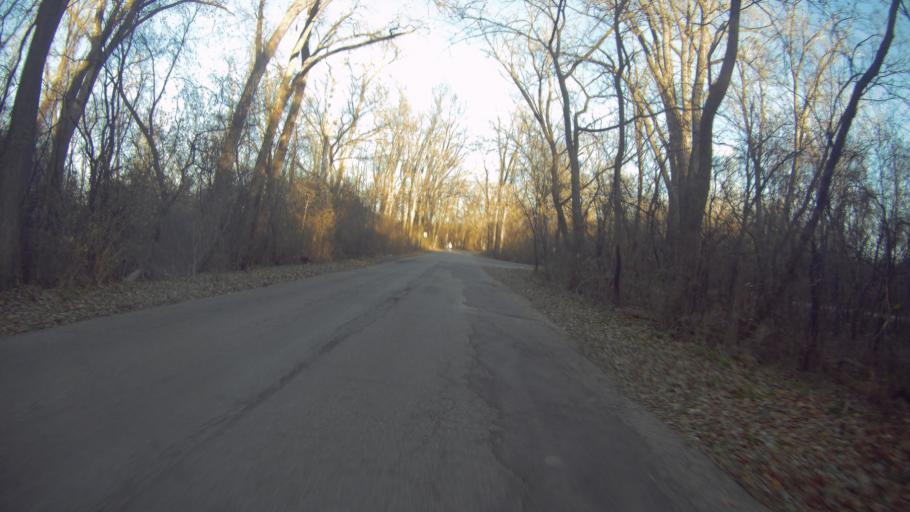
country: US
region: Wisconsin
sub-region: Dane County
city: Madison
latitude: 43.0494
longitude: -89.4167
